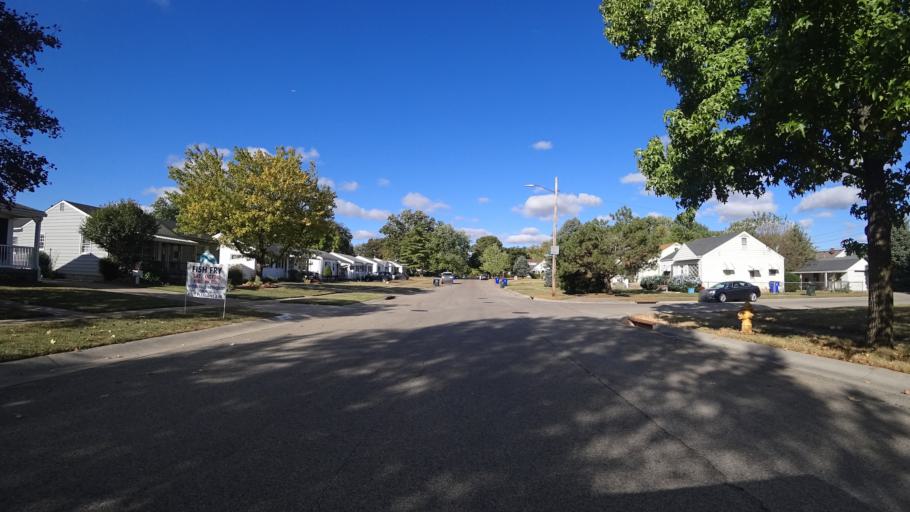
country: US
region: Ohio
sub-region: Butler County
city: Fairfield
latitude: 39.3635
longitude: -84.5496
